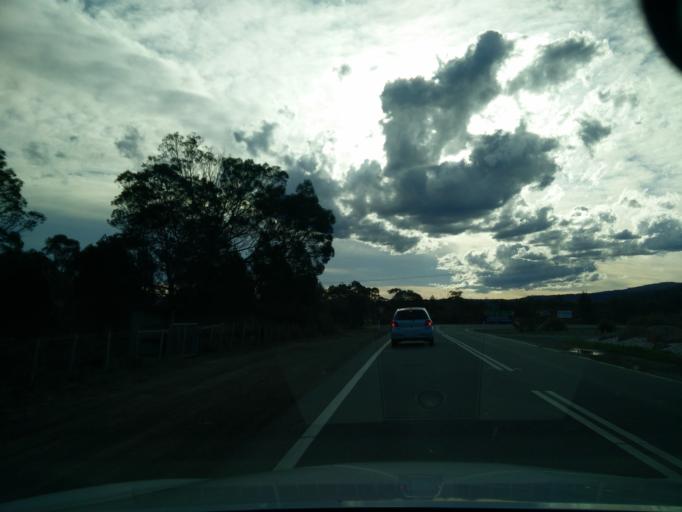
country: AU
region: Tasmania
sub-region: Break O'Day
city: St Helens
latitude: -41.9405
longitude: 148.2210
